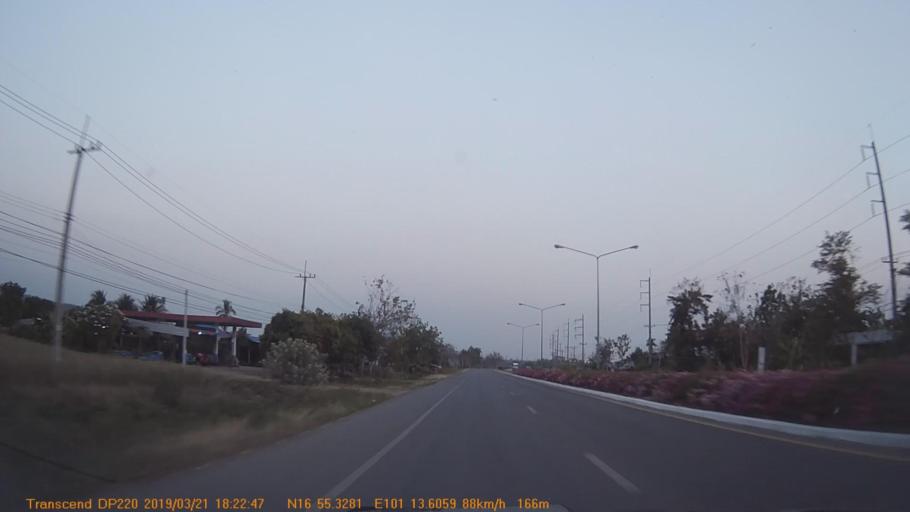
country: TH
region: Phetchabun
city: Lom Kao
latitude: 16.9218
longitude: 101.2269
